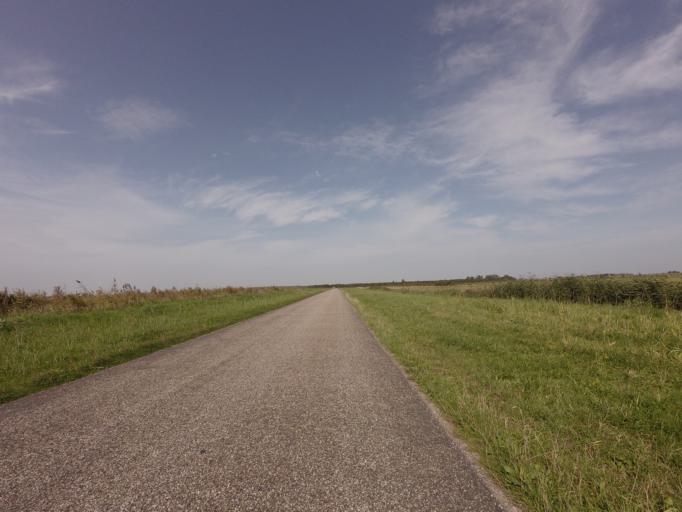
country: NL
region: Groningen
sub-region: Gemeente De Marne
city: Ulrum
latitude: 53.3502
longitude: 6.2664
